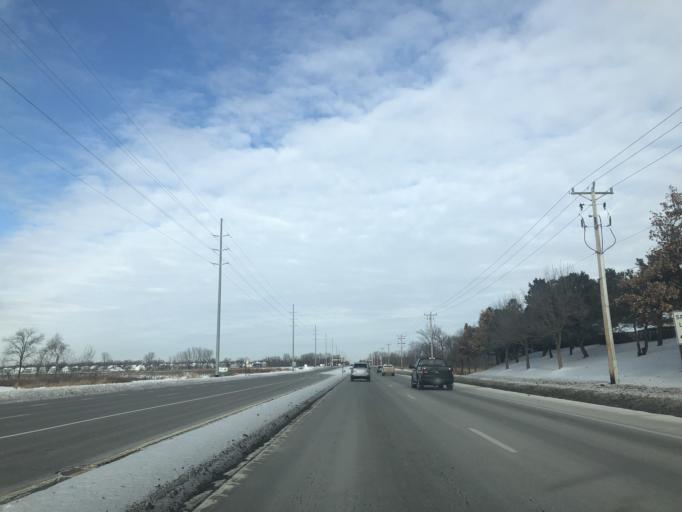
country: US
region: Minnesota
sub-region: Anoka County
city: Circle Pines
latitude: 45.1629
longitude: -93.1631
